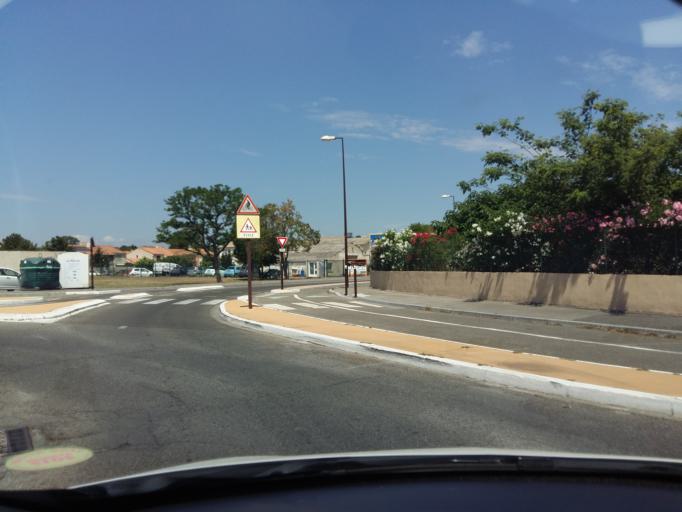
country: FR
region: Provence-Alpes-Cote d'Azur
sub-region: Departement du Vaucluse
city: Le Pontet
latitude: 43.9429
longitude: 4.8423
